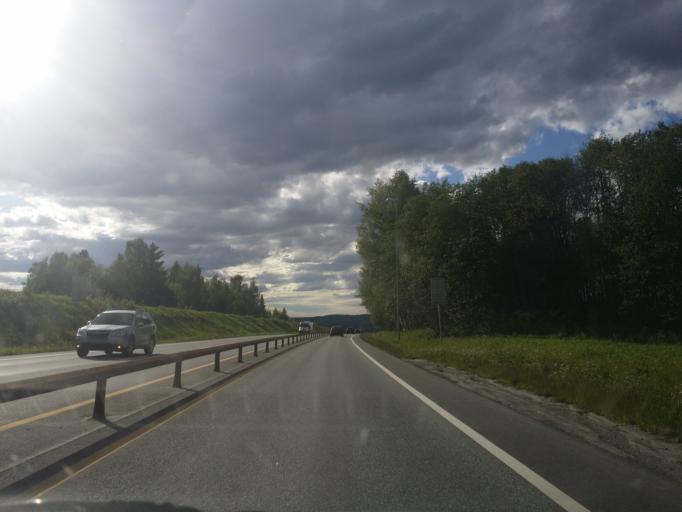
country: NO
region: Hedmark
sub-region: Stange
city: Stange
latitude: 60.7717
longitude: 11.1616
